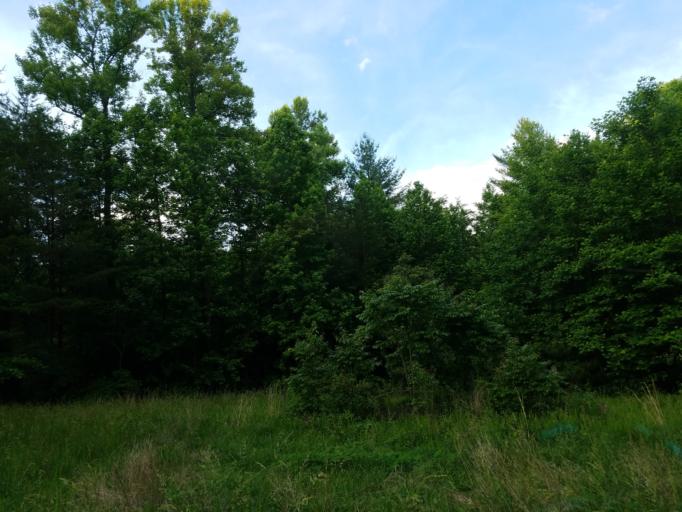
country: US
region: Georgia
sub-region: Dawson County
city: Dawsonville
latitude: 34.5804
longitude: -84.1434
